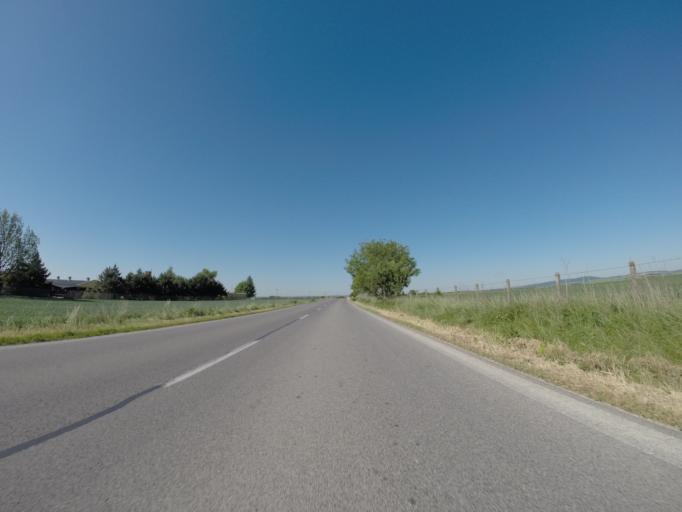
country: SK
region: Trnavsky
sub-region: Okres Trnava
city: Piestany
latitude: 48.5119
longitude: 17.9933
